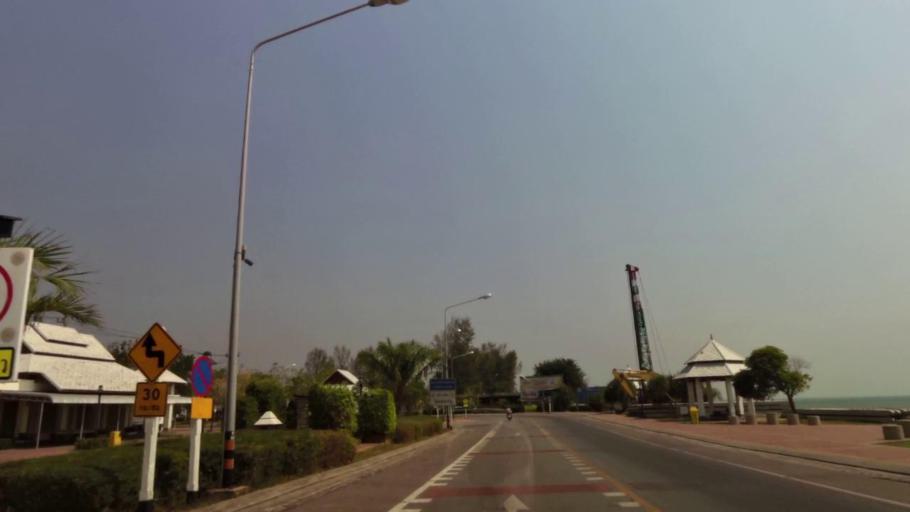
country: TH
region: Chanthaburi
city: Tha Mai
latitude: 12.5396
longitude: 101.9515
